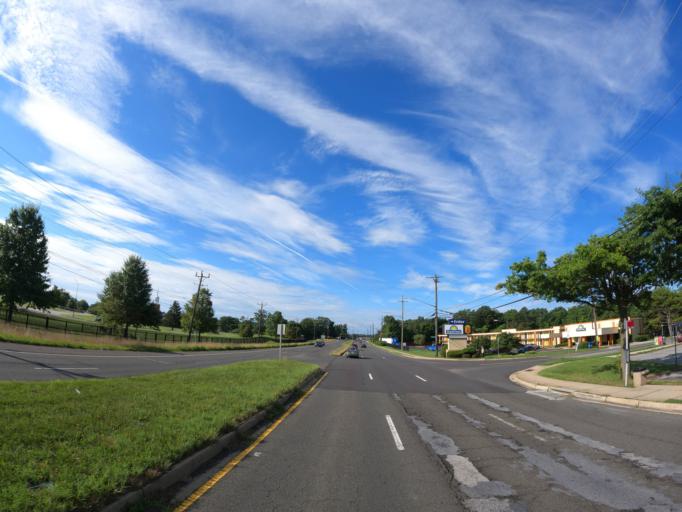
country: US
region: Maryland
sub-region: Prince George's County
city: Morningside
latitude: 38.8145
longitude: -76.8945
